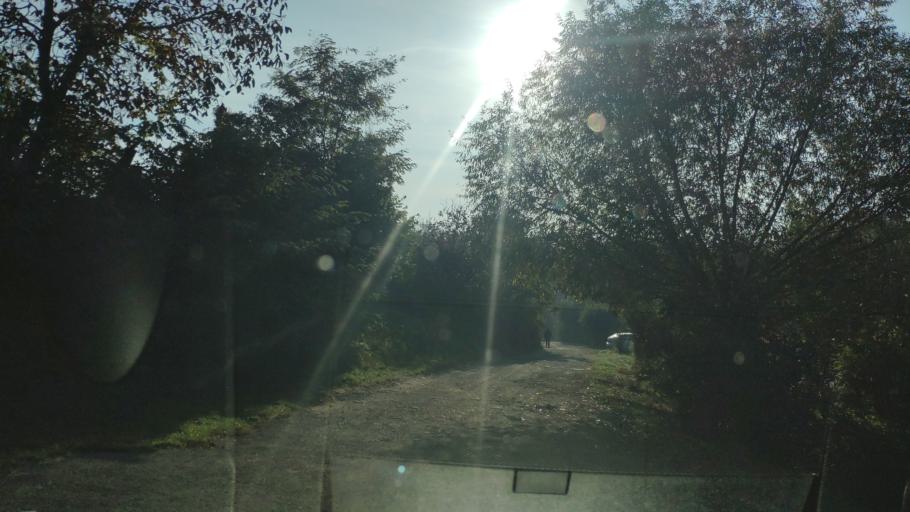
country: SK
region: Kosicky
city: Kosice
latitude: 48.7256
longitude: 21.2258
